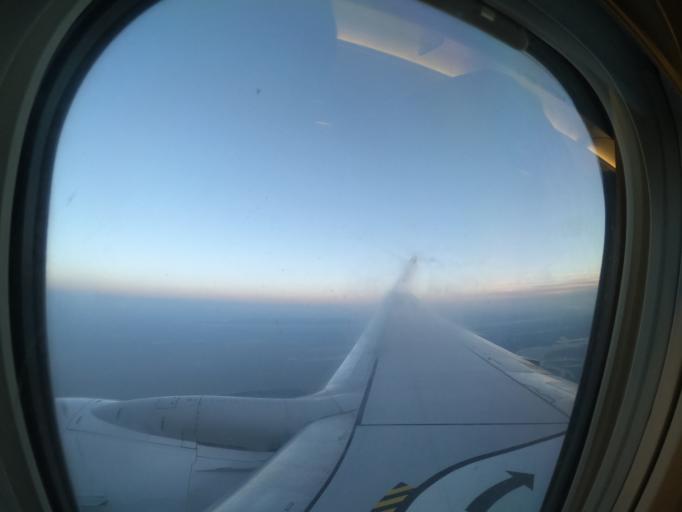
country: GB
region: England
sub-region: Essex
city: Mistley
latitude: 51.9009
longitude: 1.0873
